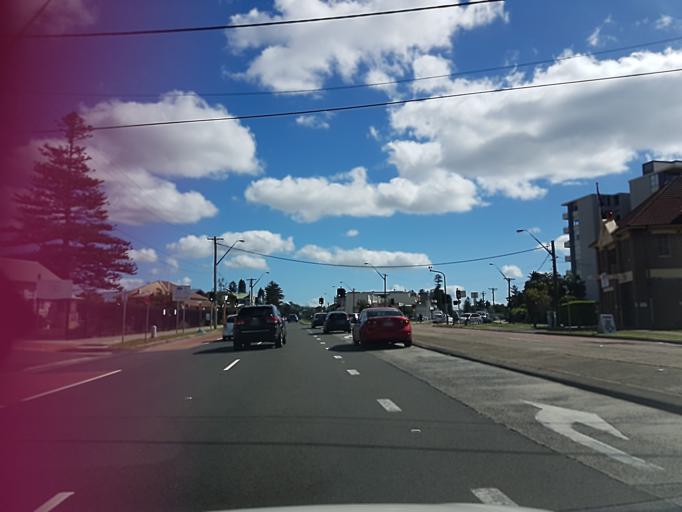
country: AU
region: New South Wales
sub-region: Warringah
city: Narrabeen
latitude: -33.7212
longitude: 151.2982
